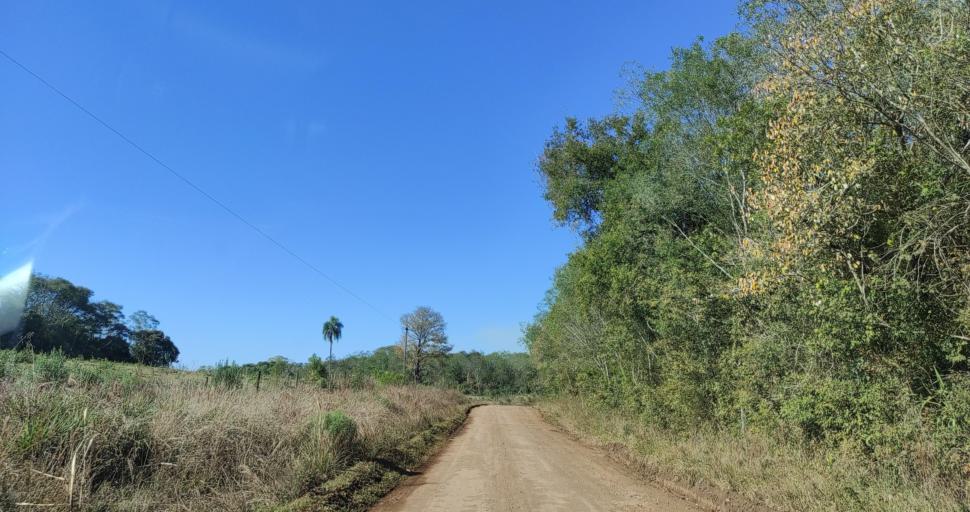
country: AR
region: Misiones
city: Cerro Cora
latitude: -27.6304
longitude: -55.6993
